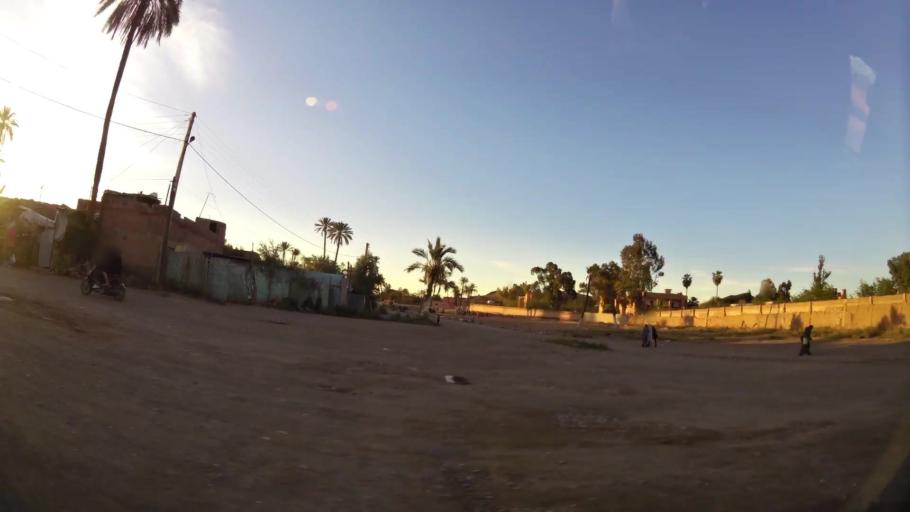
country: MA
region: Marrakech-Tensift-Al Haouz
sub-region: Marrakech
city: Marrakesh
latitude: 31.6357
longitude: -8.0330
